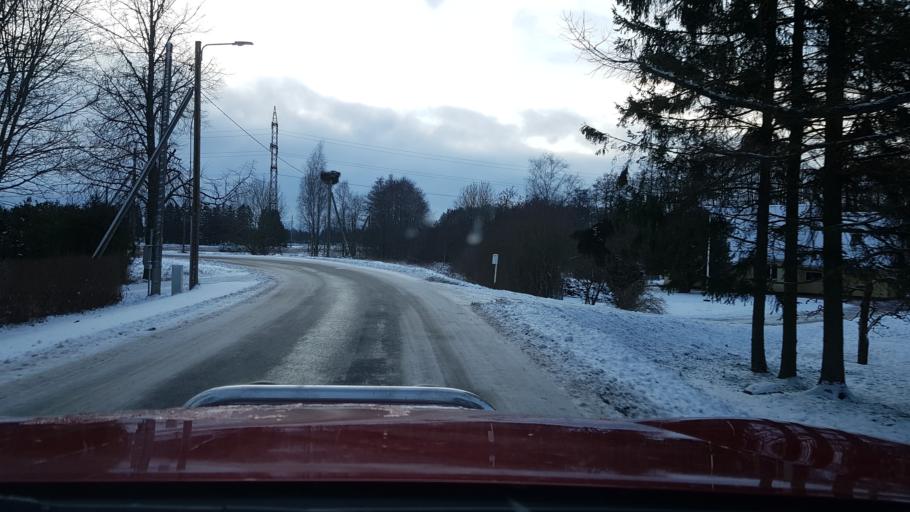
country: EE
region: Harju
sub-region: Maardu linn
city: Maardu
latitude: 59.4268
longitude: 25.0186
